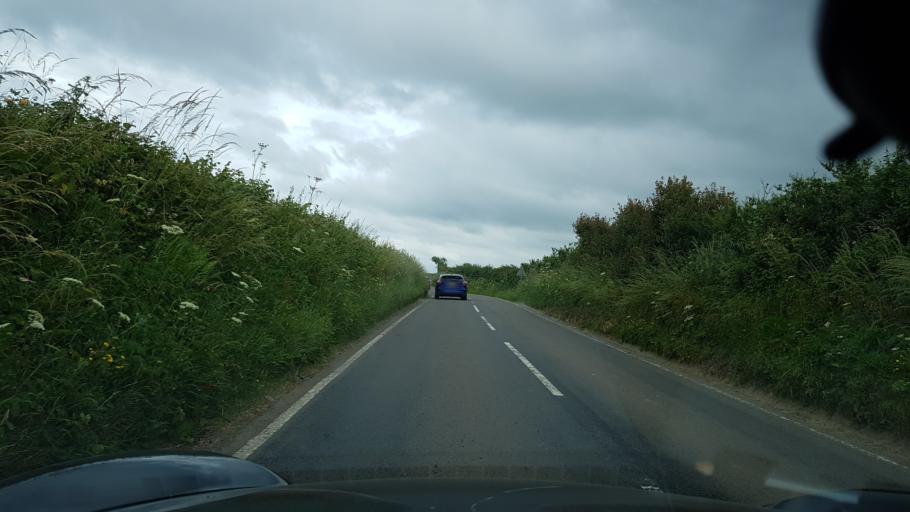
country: GB
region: Wales
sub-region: Pembrokeshire
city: Herbrandston
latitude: 51.7647
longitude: -5.0872
